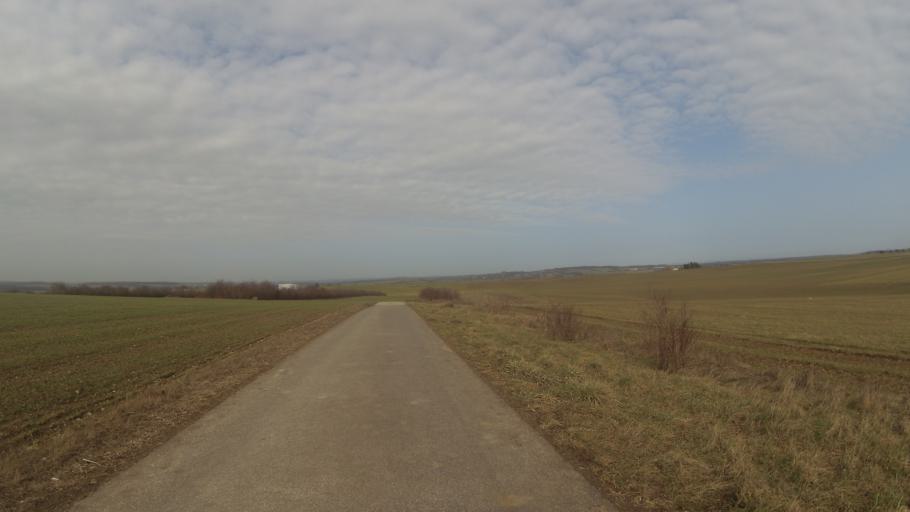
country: FR
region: Lorraine
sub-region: Departement de la Moselle
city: Merten
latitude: 49.2822
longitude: 6.6672
